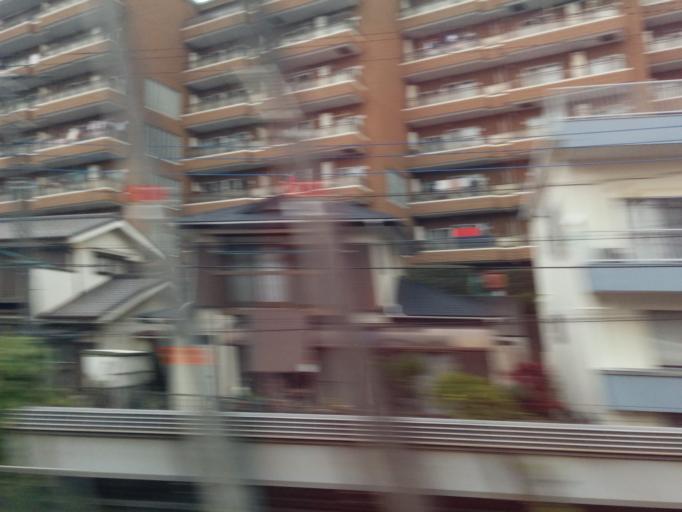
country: JP
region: Kanagawa
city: Yokohama
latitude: 35.4799
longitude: 139.5692
